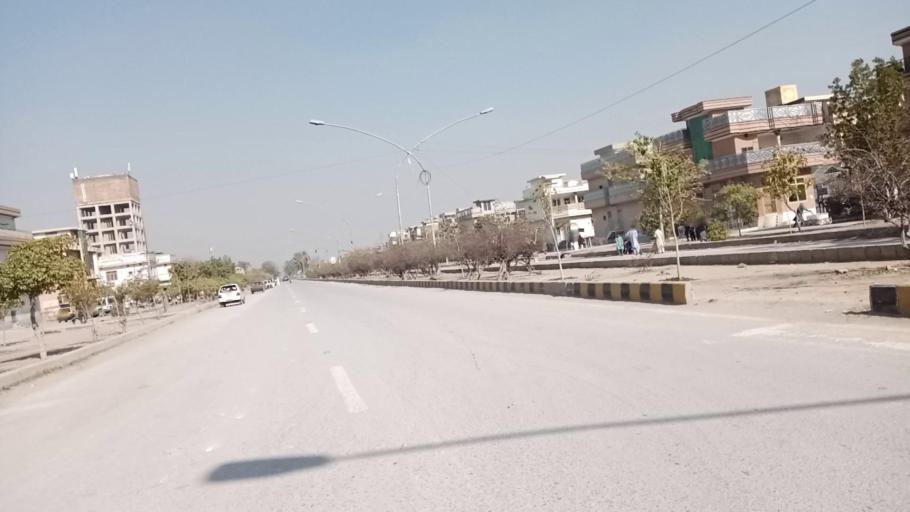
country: PK
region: Khyber Pakhtunkhwa
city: Peshawar
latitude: 33.9496
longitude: 71.4328
